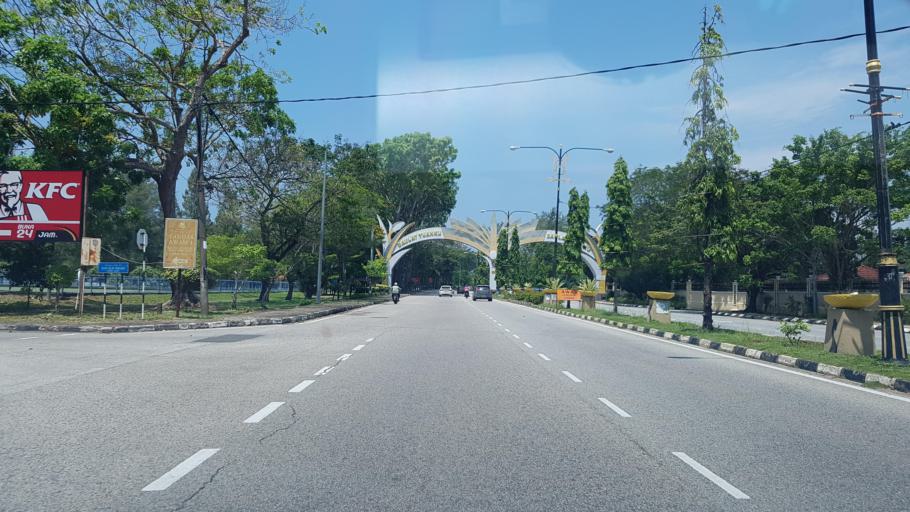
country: MY
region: Terengganu
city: Kuala Terengganu
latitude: 5.3229
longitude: 103.1514
